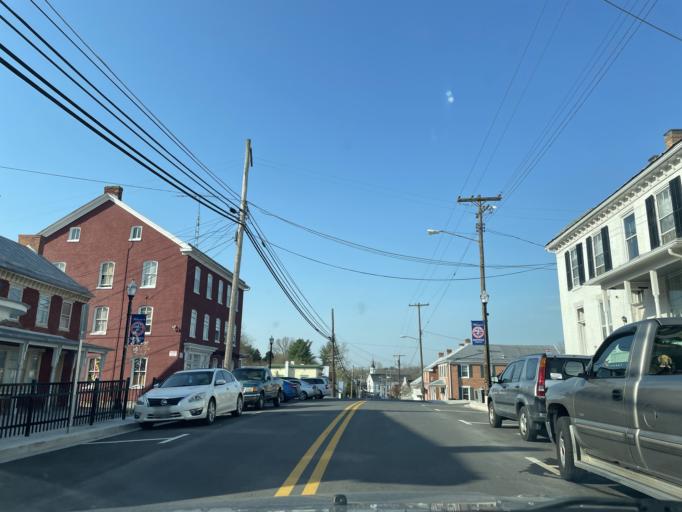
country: US
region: Maryland
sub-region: Washington County
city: Keedysville
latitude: 39.4883
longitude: -77.6984
